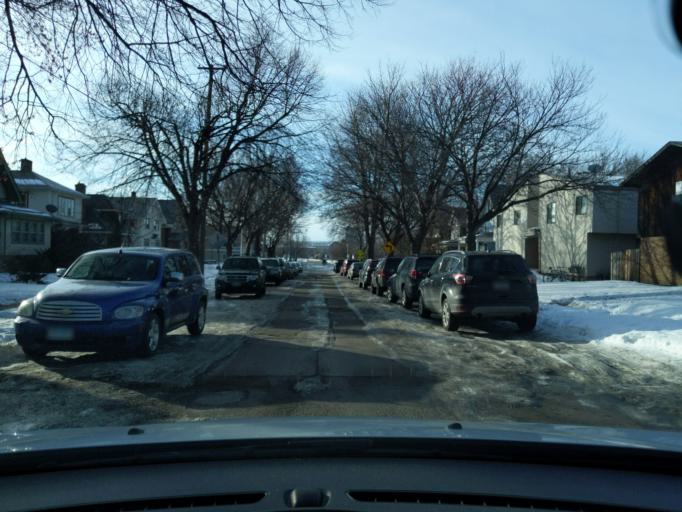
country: US
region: Minnesota
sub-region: Ramsey County
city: Lauderdale
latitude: 44.9864
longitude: -93.2290
